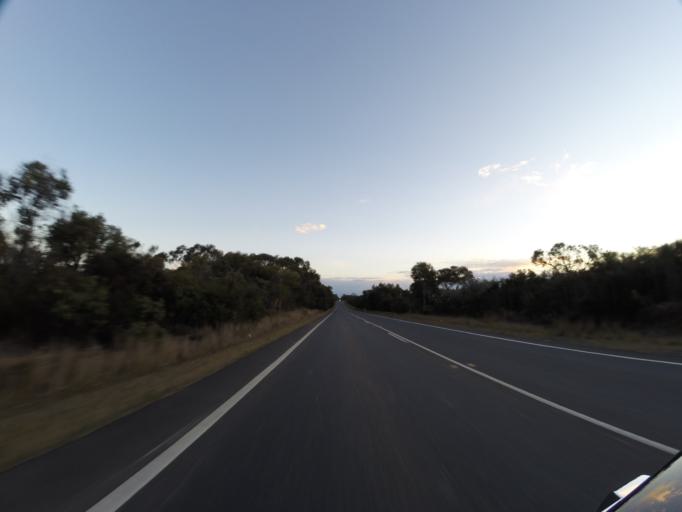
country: AU
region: New South Wales
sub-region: Sutherland Shire
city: Menai
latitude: -34.0071
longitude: 150.9904
